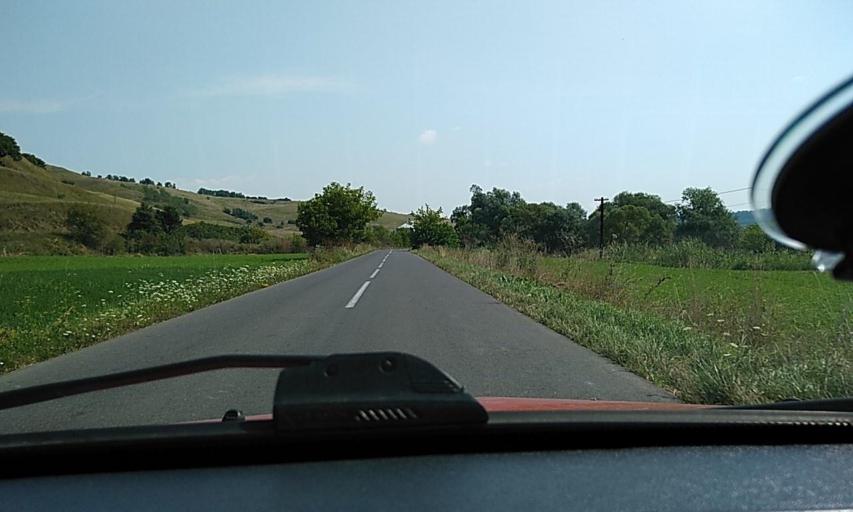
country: RO
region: Brasov
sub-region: Oras Rupea
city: Rupea
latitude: 46.0185
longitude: 25.1762
